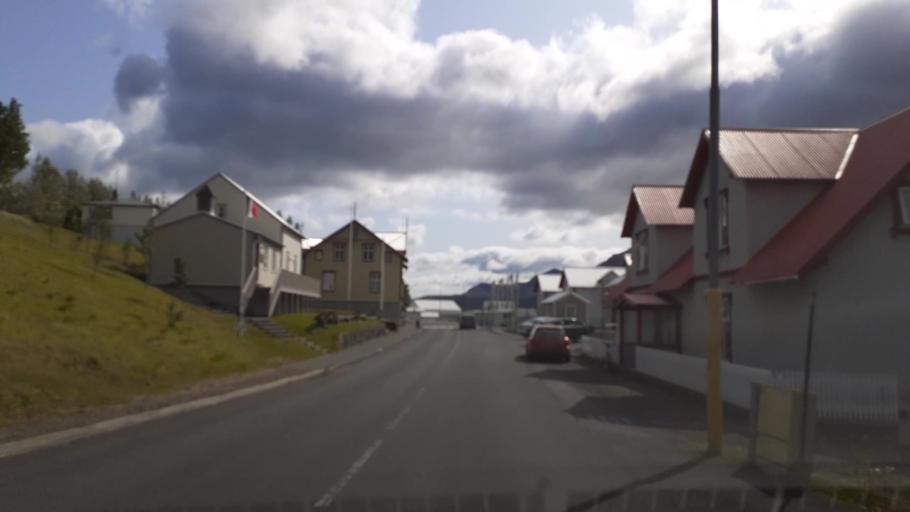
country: IS
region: East
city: Eskifjoerdur
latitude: 64.9269
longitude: -14.0022
